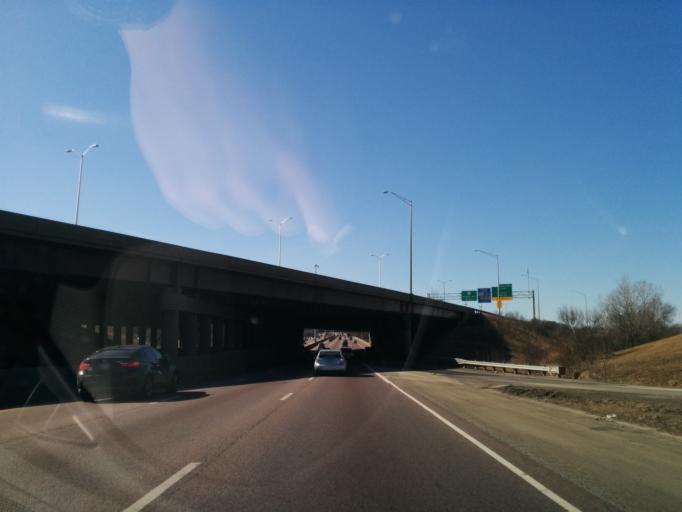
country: US
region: Illinois
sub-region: Cook County
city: Indian Head Park
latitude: 41.7610
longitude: -87.8913
